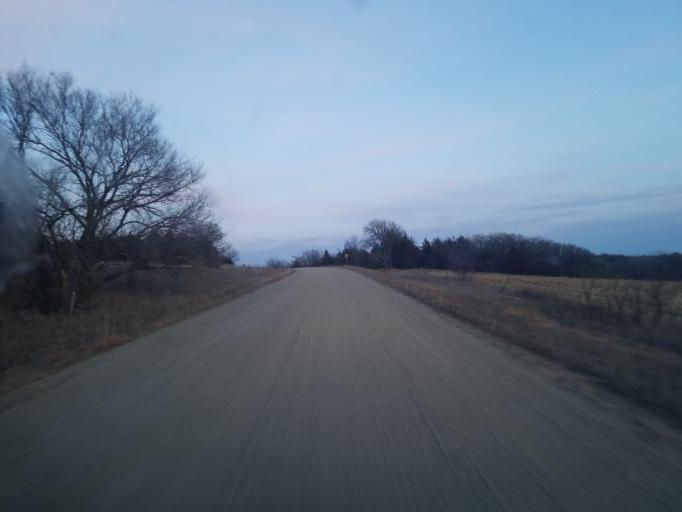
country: US
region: Nebraska
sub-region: Knox County
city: Center
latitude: 42.6102
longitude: -97.8659
